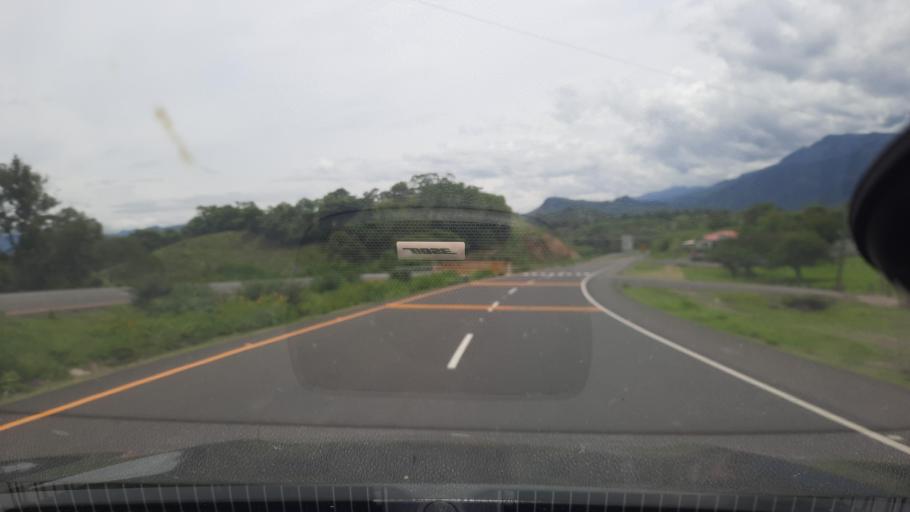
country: HN
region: Valle
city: Aramecina
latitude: 13.7524
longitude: -87.7162
